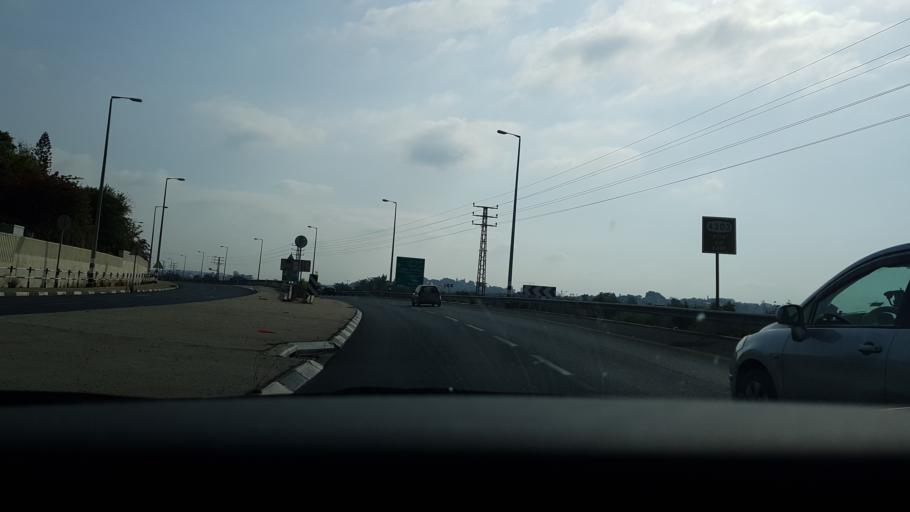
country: IL
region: Central District
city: Ness Ziona
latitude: 31.9202
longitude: 34.7726
